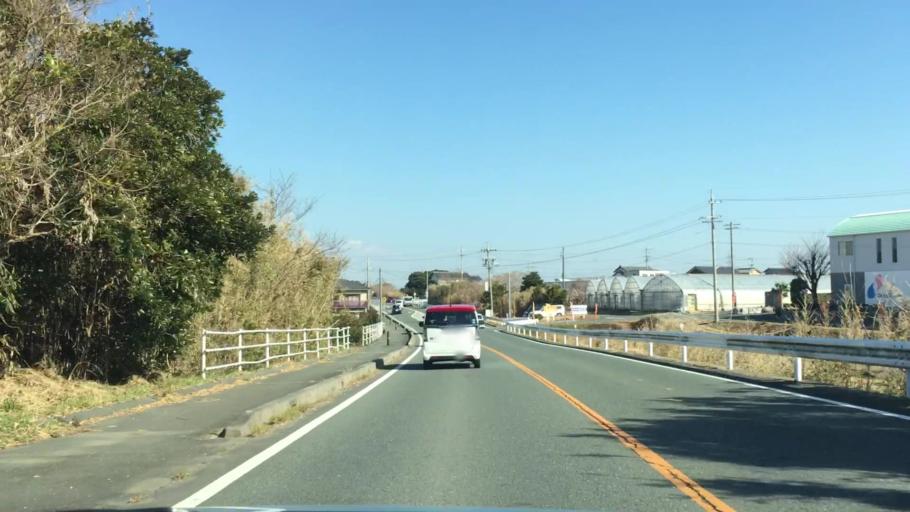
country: JP
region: Aichi
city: Tahara
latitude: 34.6655
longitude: 137.2840
